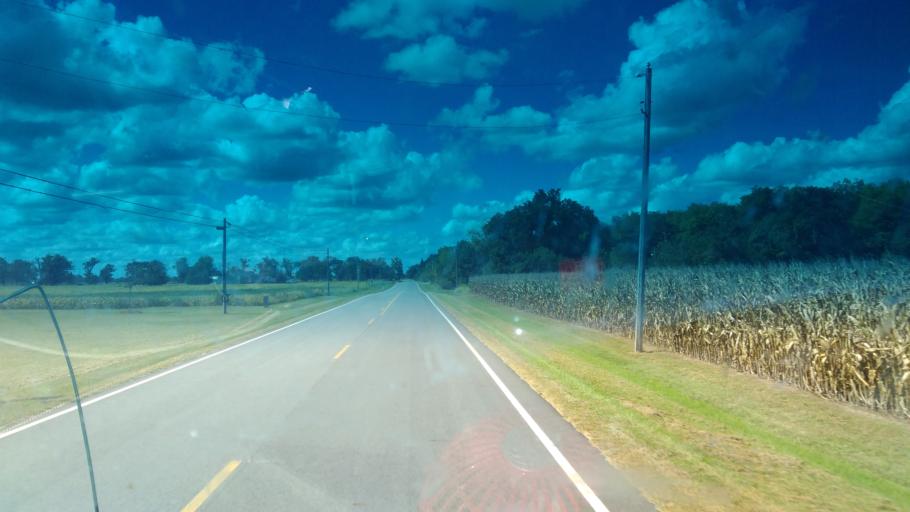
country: US
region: Ohio
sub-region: Champaign County
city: North Lewisburg
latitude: 40.1900
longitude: -83.4657
